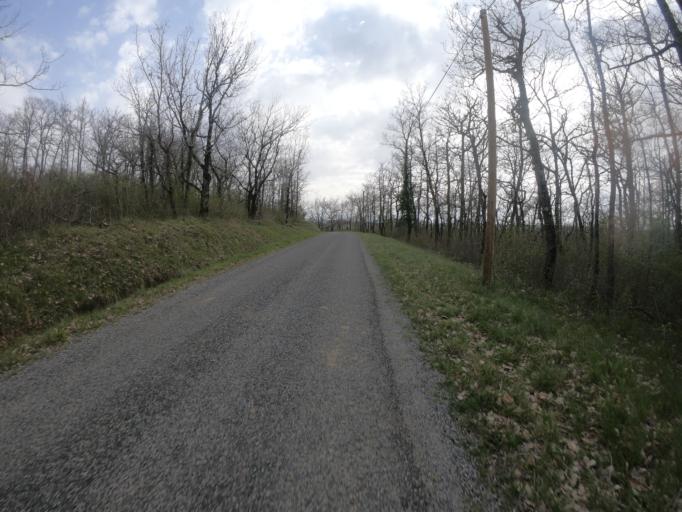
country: FR
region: Languedoc-Roussillon
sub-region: Departement de l'Aude
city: Belpech
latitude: 43.1263
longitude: 1.7427
